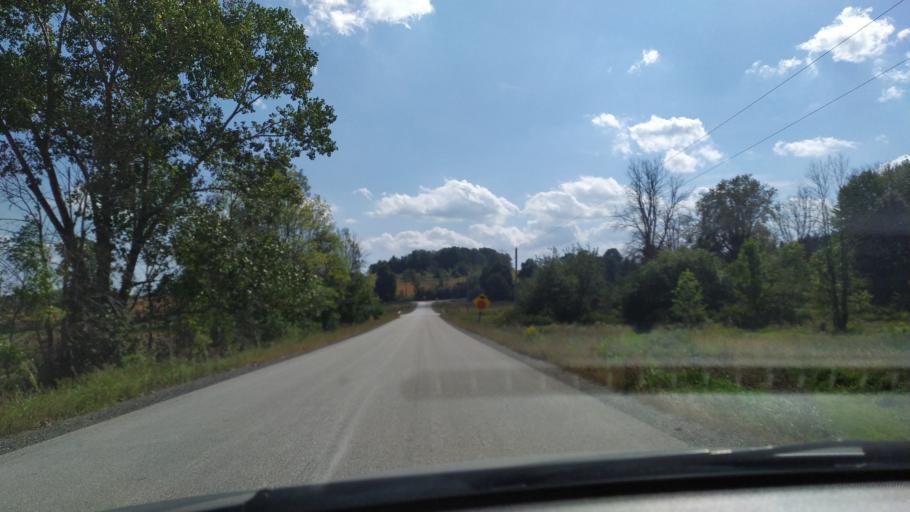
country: CA
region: Ontario
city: Stratford
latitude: 43.2933
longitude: -80.9387
